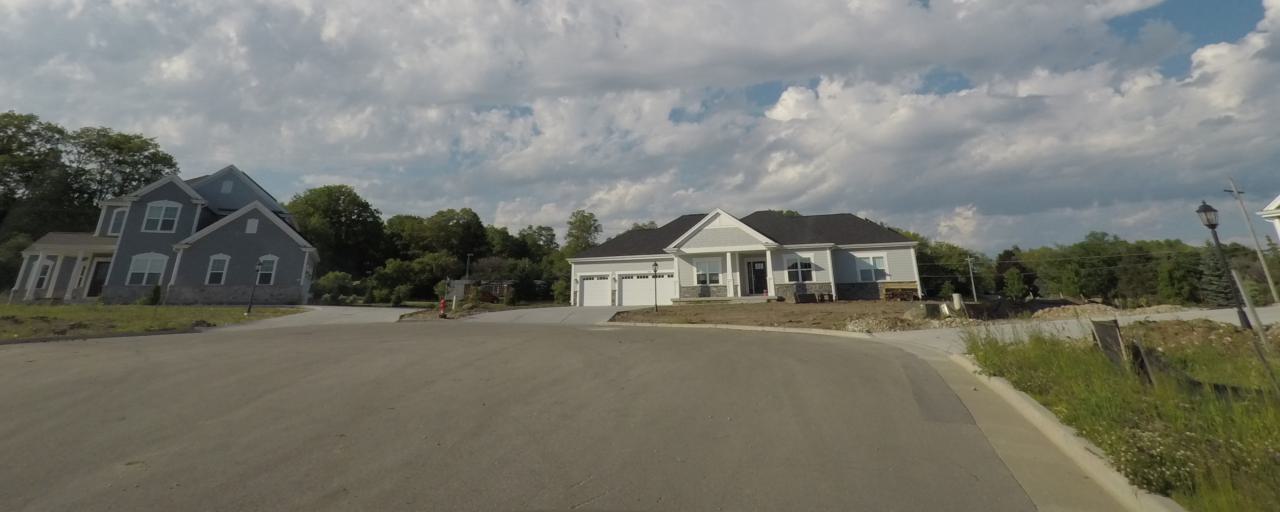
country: US
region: Wisconsin
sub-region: Waukesha County
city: New Berlin
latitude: 42.9434
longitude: -88.0904
